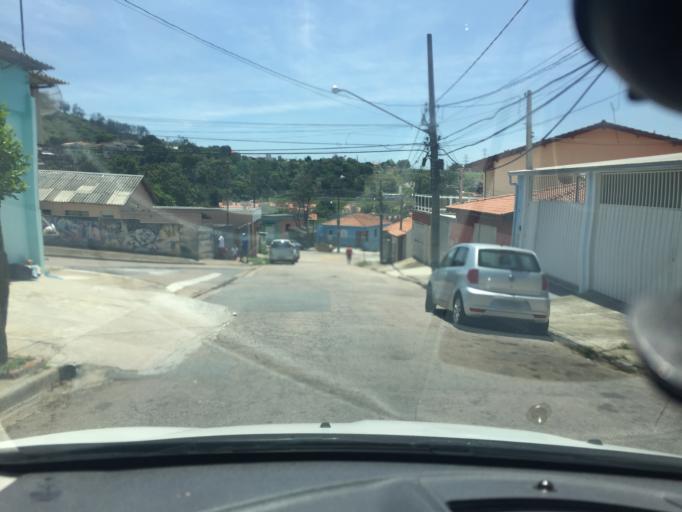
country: BR
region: Sao Paulo
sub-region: Jundiai
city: Jundiai
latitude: -23.2254
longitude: -46.8790
